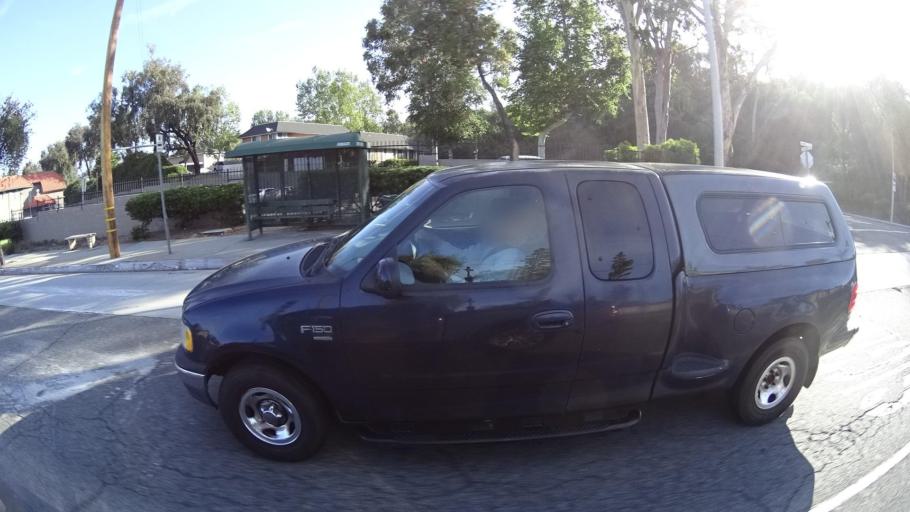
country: US
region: California
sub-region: Los Angeles County
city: South San Jose Hills
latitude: 34.0343
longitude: -117.9176
